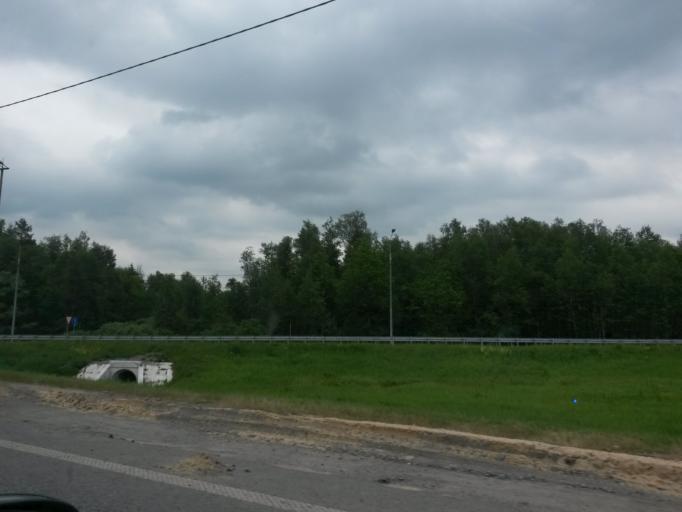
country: RU
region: Moskovskaya
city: Lyubuchany
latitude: 55.1882
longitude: 37.5348
